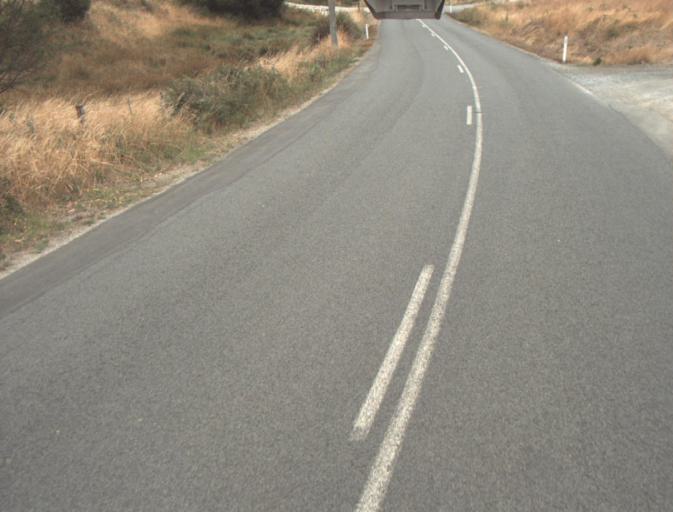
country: AU
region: Tasmania
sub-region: Launceston
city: Mayfield
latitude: -41.1873
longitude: 147.2221
